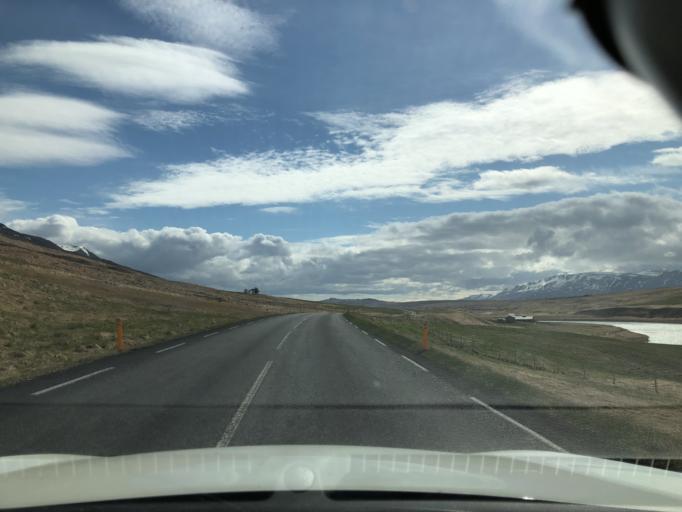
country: IS
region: Northwest
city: Saudarkrokur
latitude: 65.6411
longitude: -20.1635
